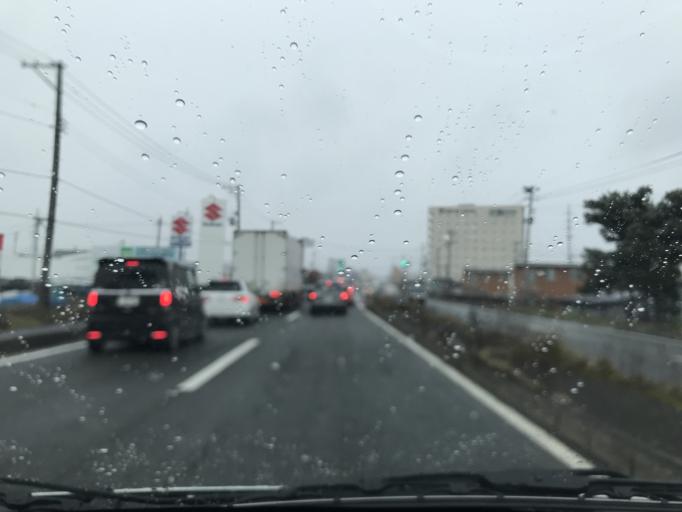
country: JP
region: Iwate
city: Kitakami
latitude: 39.2840
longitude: 141.1028
